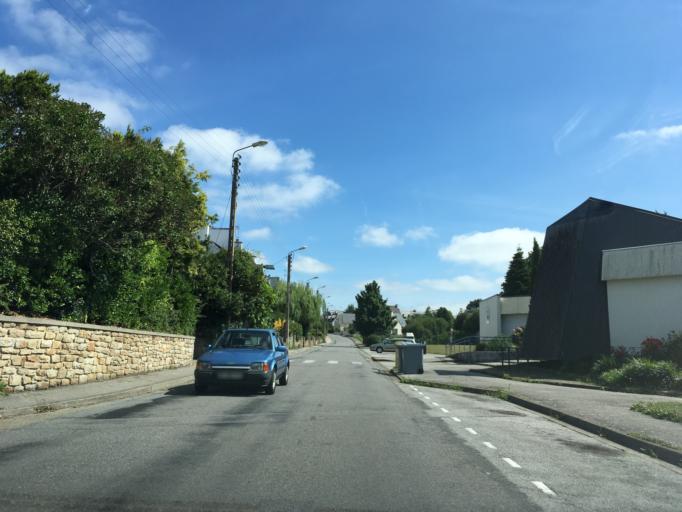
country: FR
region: Brittany
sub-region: Departement du Finistere
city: Quimper
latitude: 48.0027
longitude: -4.0942
